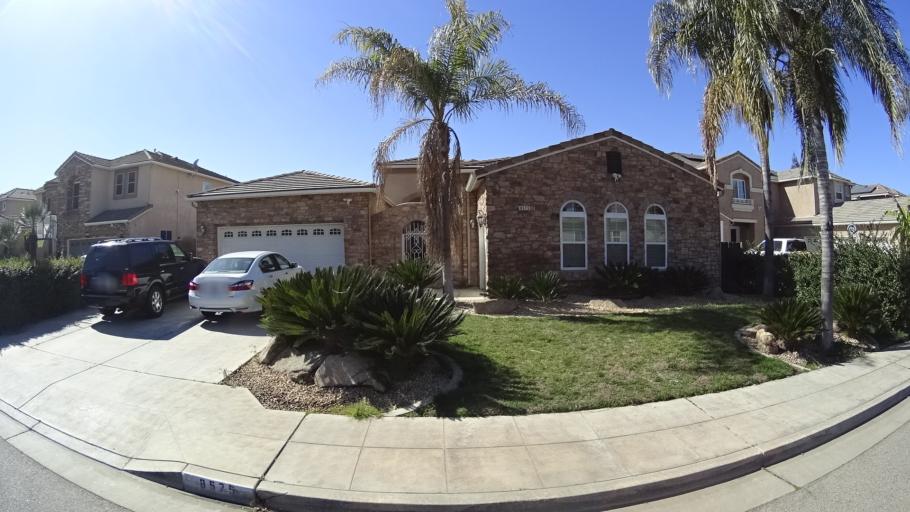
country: US
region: California
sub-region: Fresno County
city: Clovis
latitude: 36.8607
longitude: -119.7338
